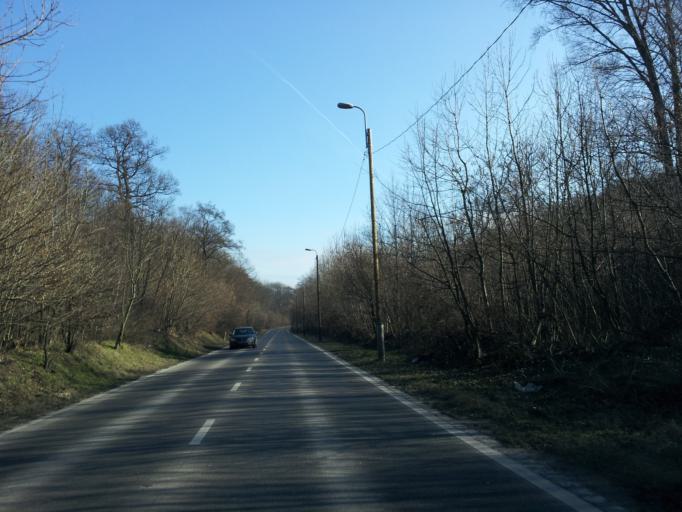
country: HU
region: Pest
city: Budakeszi
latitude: 47.5392
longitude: 18.9595
